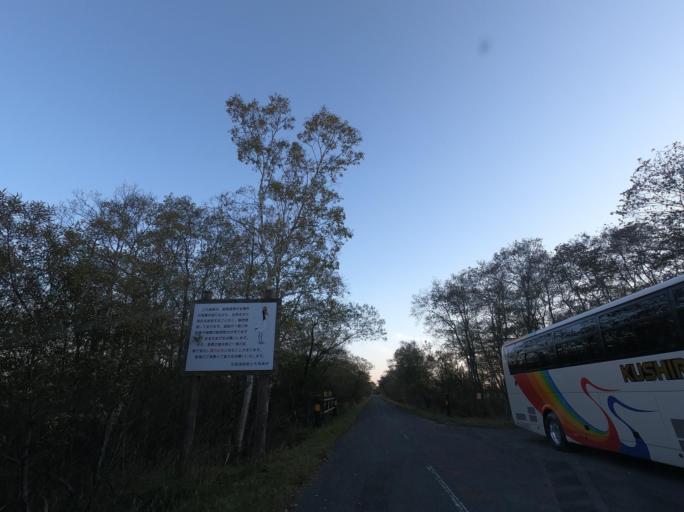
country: JP
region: Hokkaido
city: Kushiro
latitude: 43.1910
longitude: 144.4663
